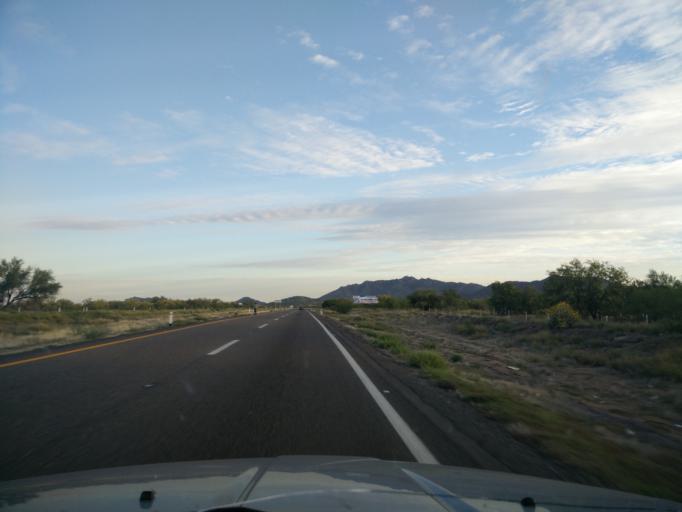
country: MX
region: Sonora
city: Hermosillo
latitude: 28.9203
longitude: -110.9523
